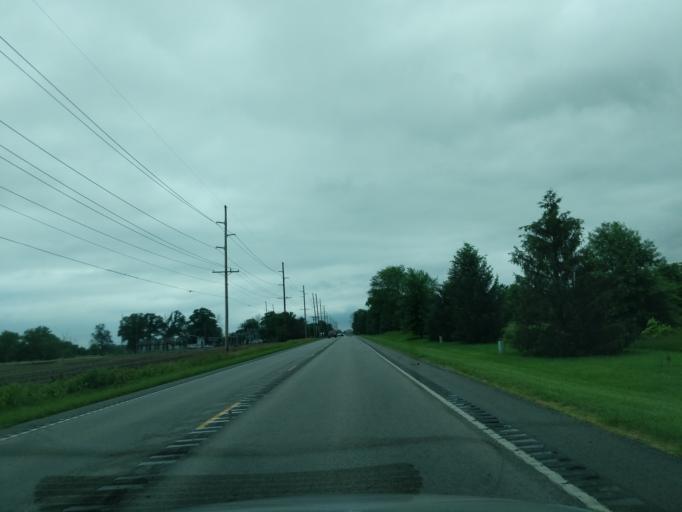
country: US
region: Indiana
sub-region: Hamilton County
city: Cicero
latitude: 40.0993
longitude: -86.0139
